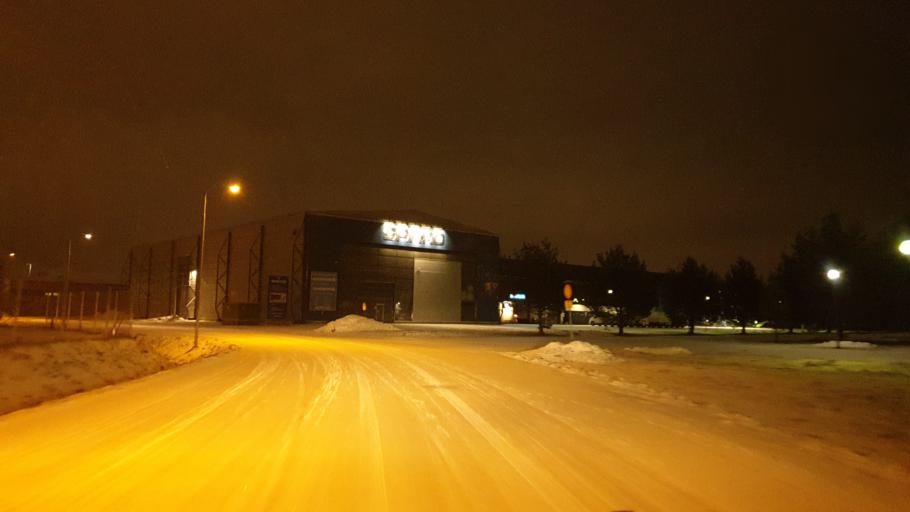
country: FI
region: Northern Ostrobothnia
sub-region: Oulu
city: Oulu
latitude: 64.9934
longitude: 25.4509
